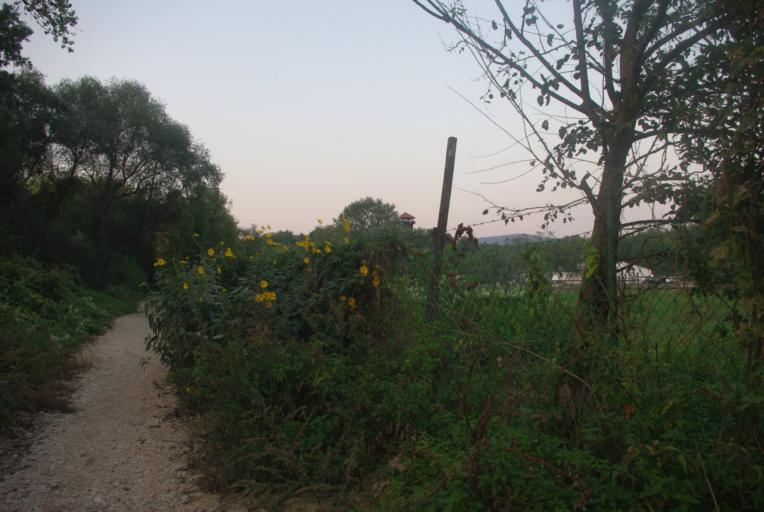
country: HU
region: Pest
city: Solymar
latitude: 47.5901
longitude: 18.9477
